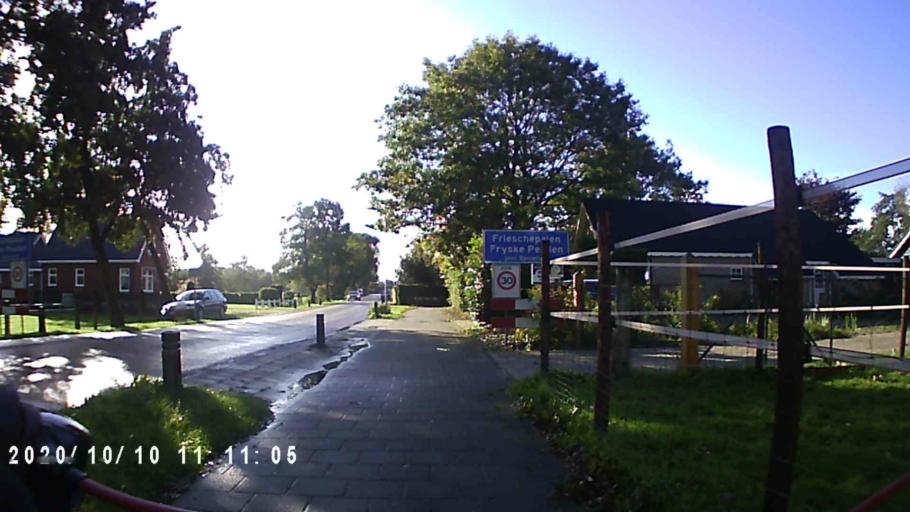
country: NL
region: Friesland
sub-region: Gemeente Smallingerland
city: Drachtstercompagnie
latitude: 53.1144
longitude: 6.2061
